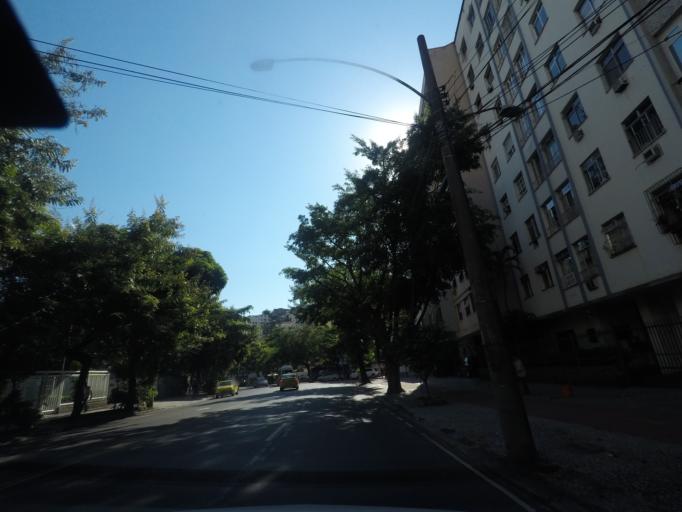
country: BR
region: Rio de Janeiro
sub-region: Rio De Janeiro
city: Rio de Janeiro
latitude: -22.9382
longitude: -43.1921
